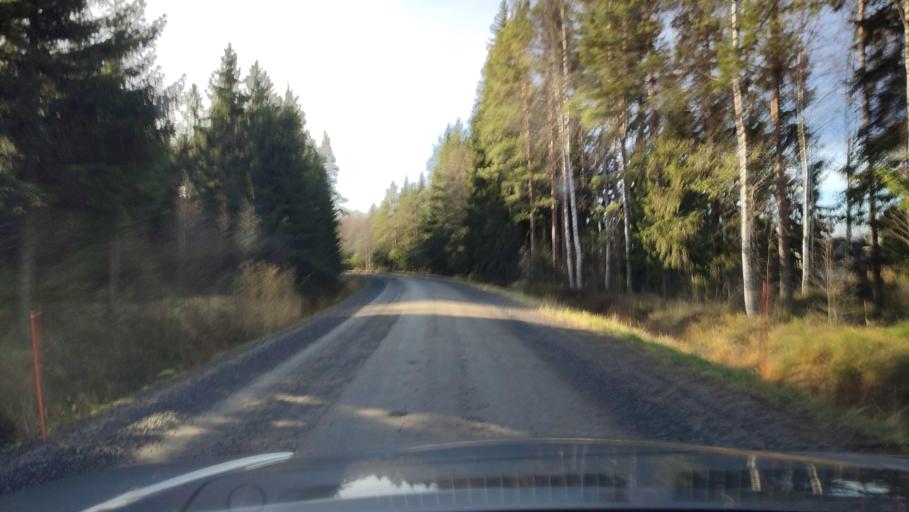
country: FI
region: Southern Ostrobothnia
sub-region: Suupohja
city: Teuva
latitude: 62.4531
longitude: 21.6155
